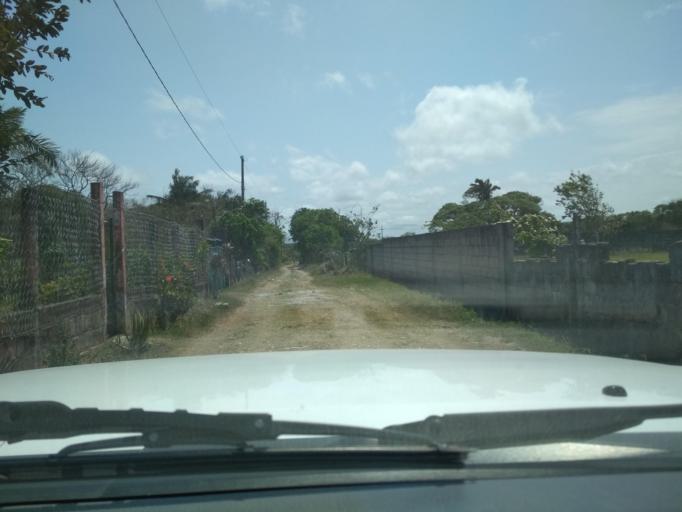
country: MX
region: Veracruz
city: Anton Lizardo
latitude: 19.0039
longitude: -95.9927
